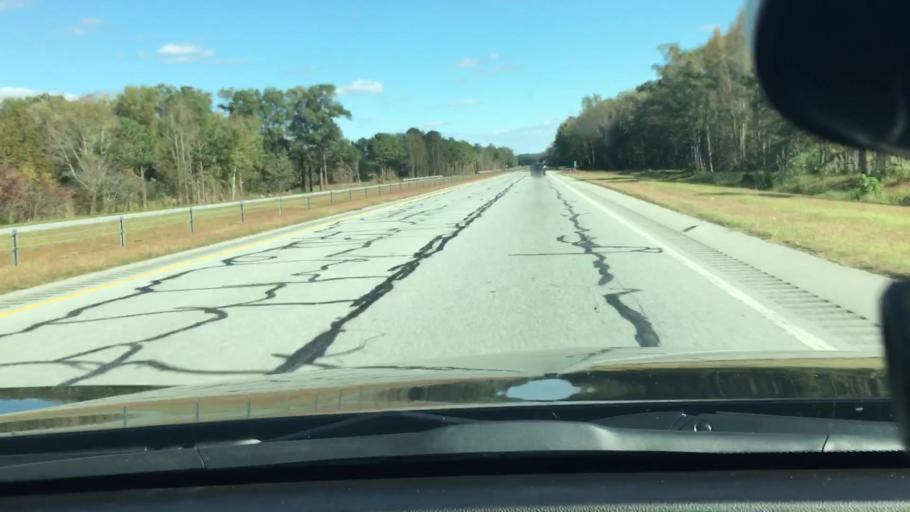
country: US
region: North Carolina
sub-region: Pitt County
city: Farmville
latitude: 35.6161
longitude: -77.6398
